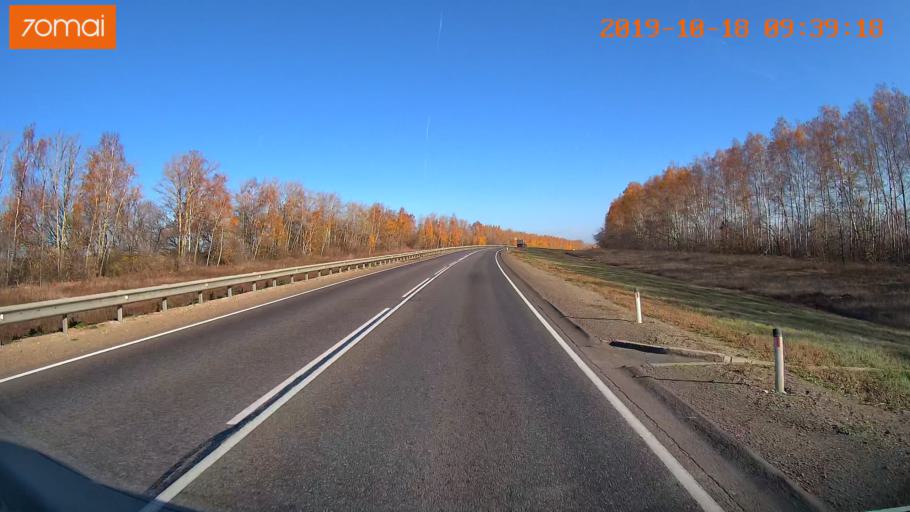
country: RU
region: Tula
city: Yefremov
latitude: 53.2513
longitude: 38.1345
